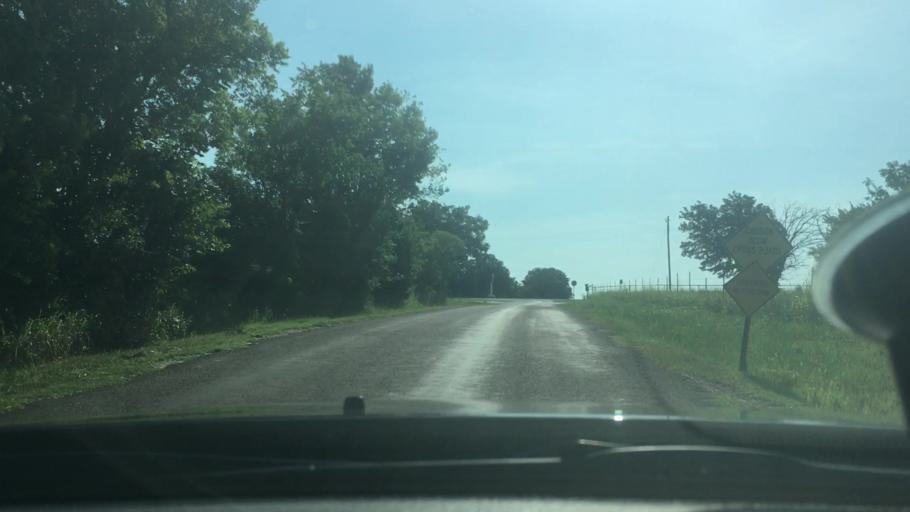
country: US
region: Oklahoma
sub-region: Garvin County
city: Pauls Valley
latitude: 34.6521
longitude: -97.3538
